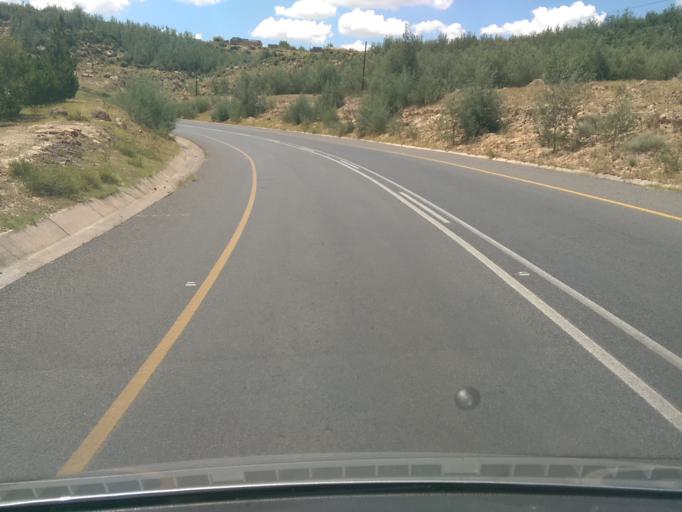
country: LS
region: Maseru
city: Maseru
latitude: -29.3962
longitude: 27.5297
